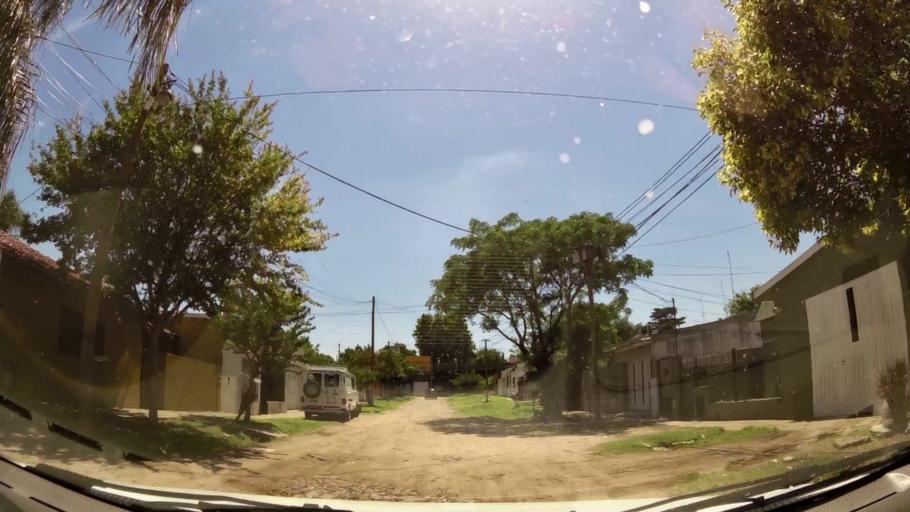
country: AR
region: Buenos Aires
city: Ituzaingo
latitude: -34.6712
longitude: -58.6866
